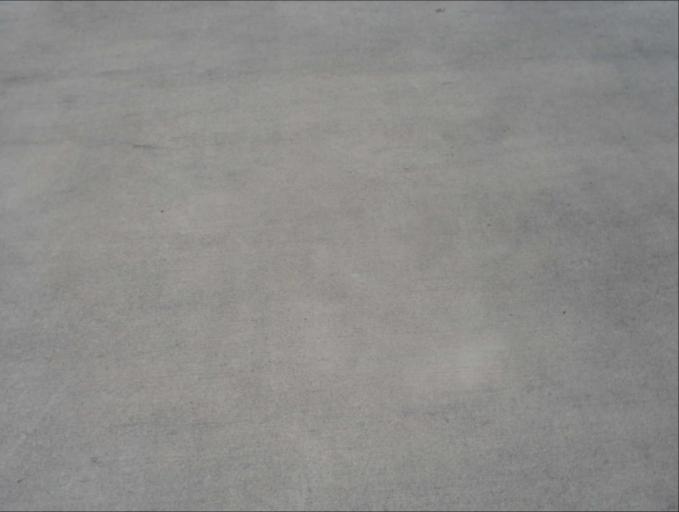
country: AU
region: Queensland
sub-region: Logan
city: Slacks Creek
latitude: -27.6391
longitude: 153.1378
